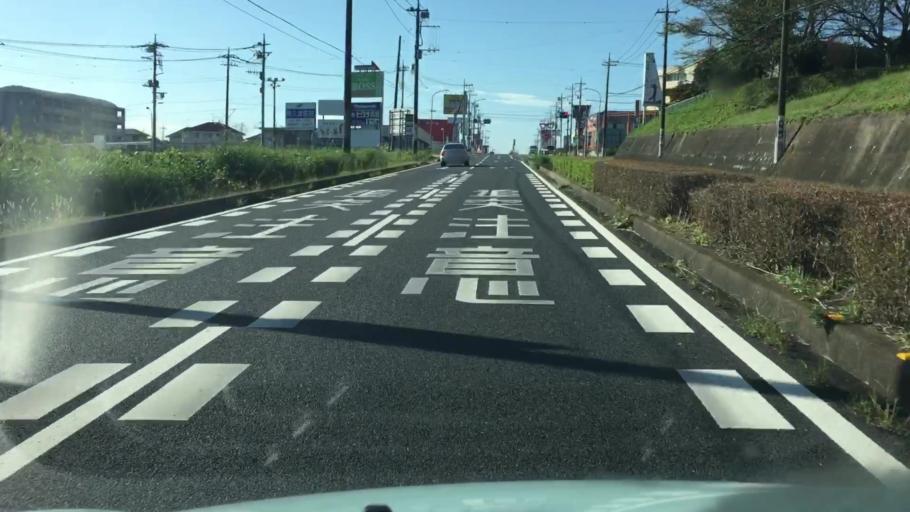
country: JP
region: Tochigi
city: Ujiie
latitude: 36.6251
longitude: 139.9927
